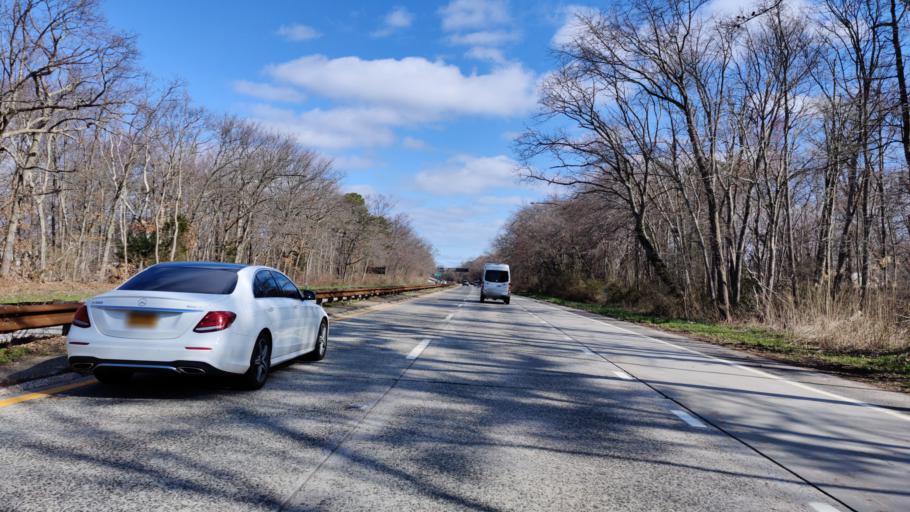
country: US
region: New York
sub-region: Suffolk County
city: West Bay Shore
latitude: 40.7028
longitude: -73.2885
